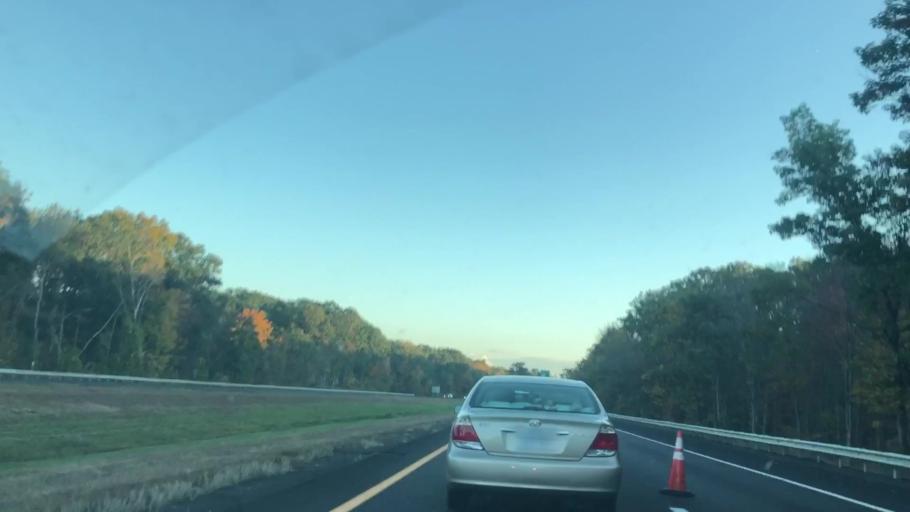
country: US
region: Massachusetts
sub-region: Franklin County
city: South Deerfield
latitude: 42.4954
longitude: -72.6174
